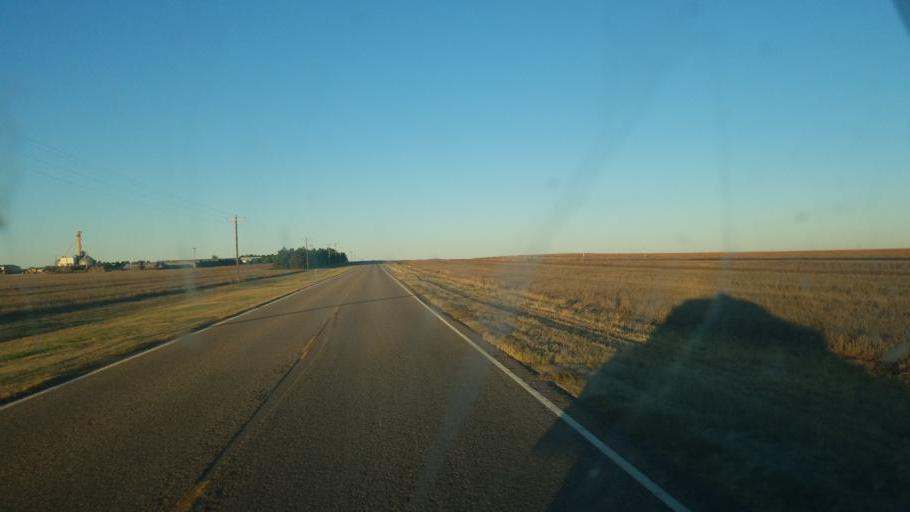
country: US
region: Colorado
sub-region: Cheyenne County
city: Cheyenne Wells
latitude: 38.8535
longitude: -102.0725
